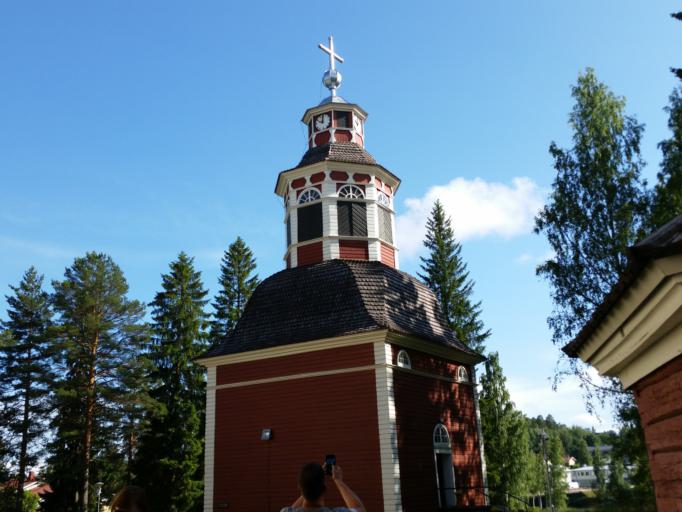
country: FI
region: Southern Savonia
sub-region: Savonlinna
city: Sulkava
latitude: 61.7894
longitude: 28.3735
